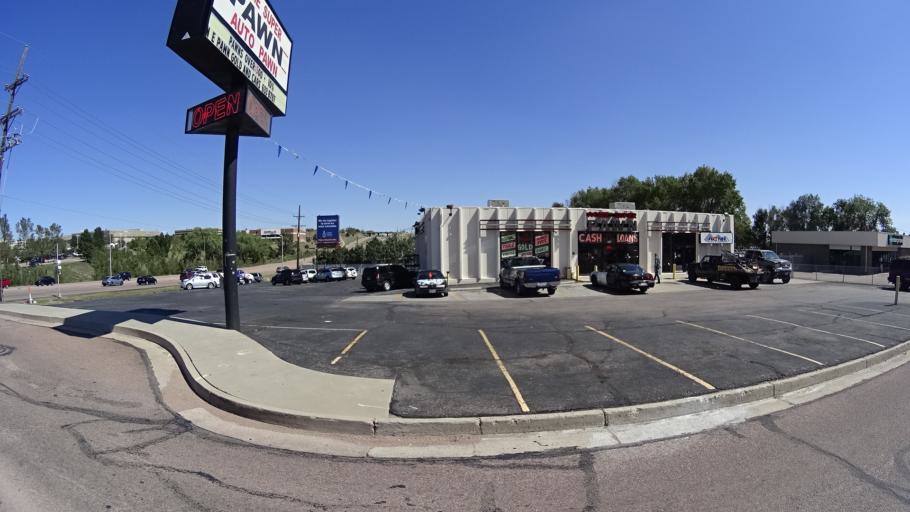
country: US
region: Colorado
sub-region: El Paso County
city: Colorado Springs
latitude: 38.8393
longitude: -104.7666
